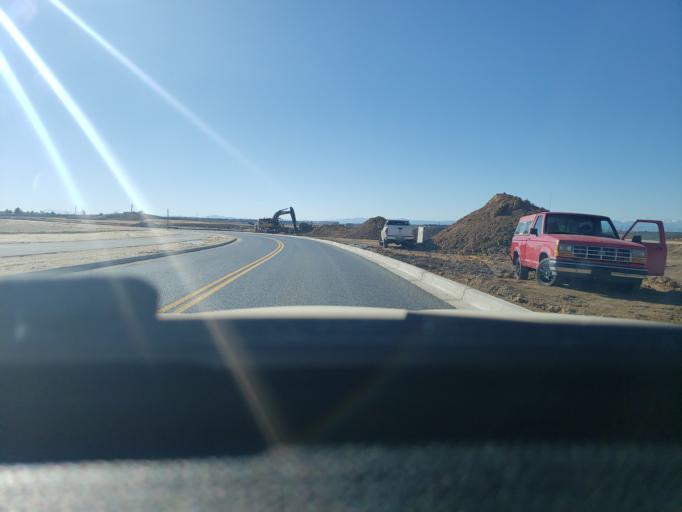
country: US
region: Colorado
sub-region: Adams County
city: Aurora
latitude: 39.7618
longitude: -104.7124
